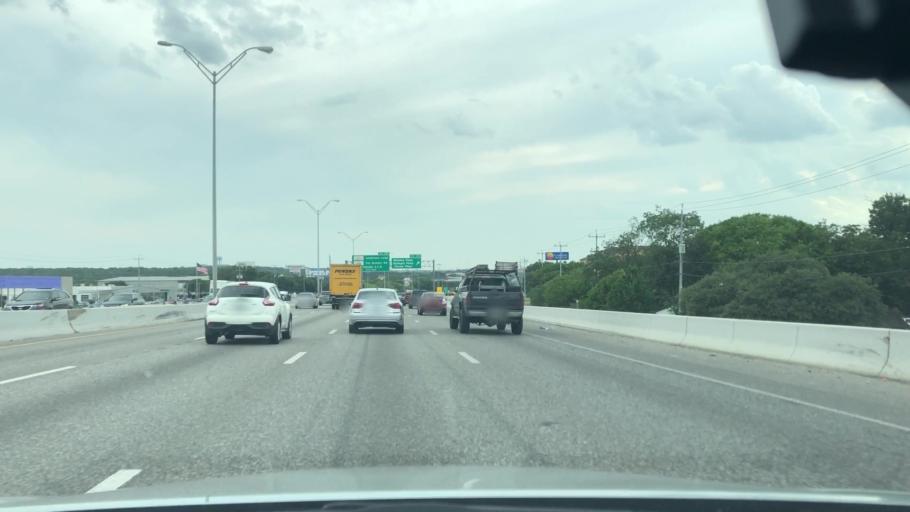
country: US
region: Texas
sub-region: Bexar County
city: Selma
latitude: 29.5841
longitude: -98.3068
